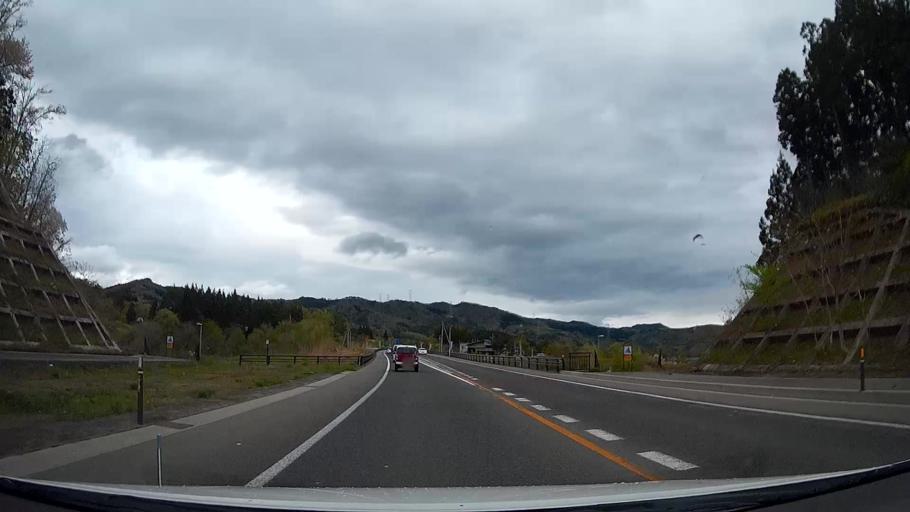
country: JP
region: Yamagata
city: Kaminoyama
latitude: 38.1114
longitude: 140.2112
